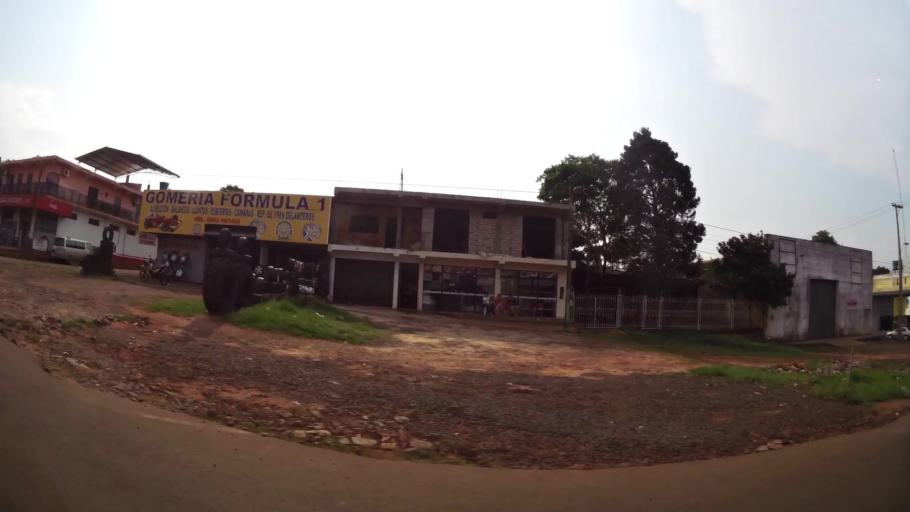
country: PY
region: Alto Parana
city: Ciudad del Este
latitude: -25.4950
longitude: -54.6619
